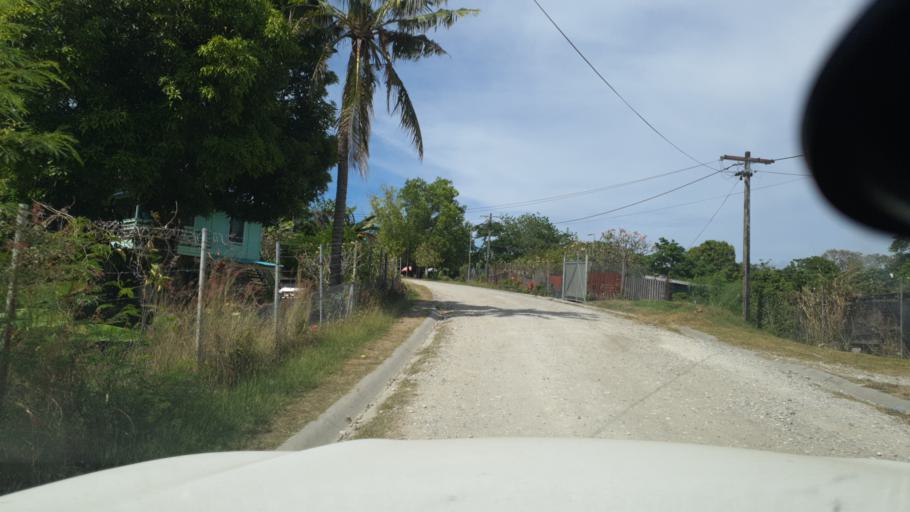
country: SB
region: Guadalcanal
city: Honiara
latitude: -9.4418
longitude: 159.9734
